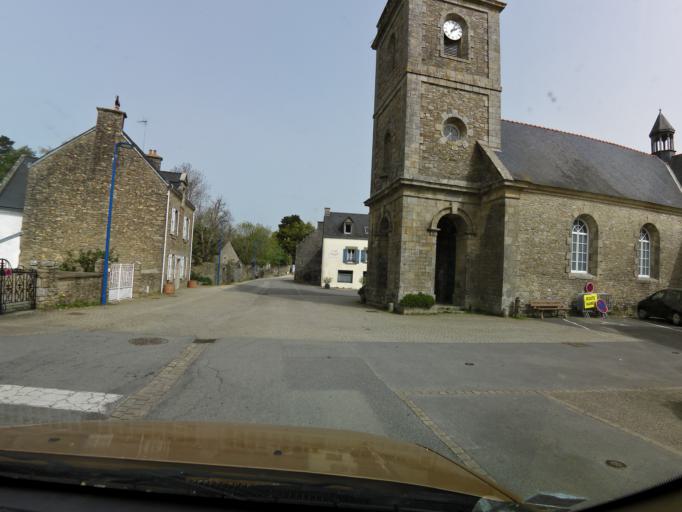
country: FR
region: Brittany
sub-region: Departement du Morbihan
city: Sene
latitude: 47.5729
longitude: -2.7099
